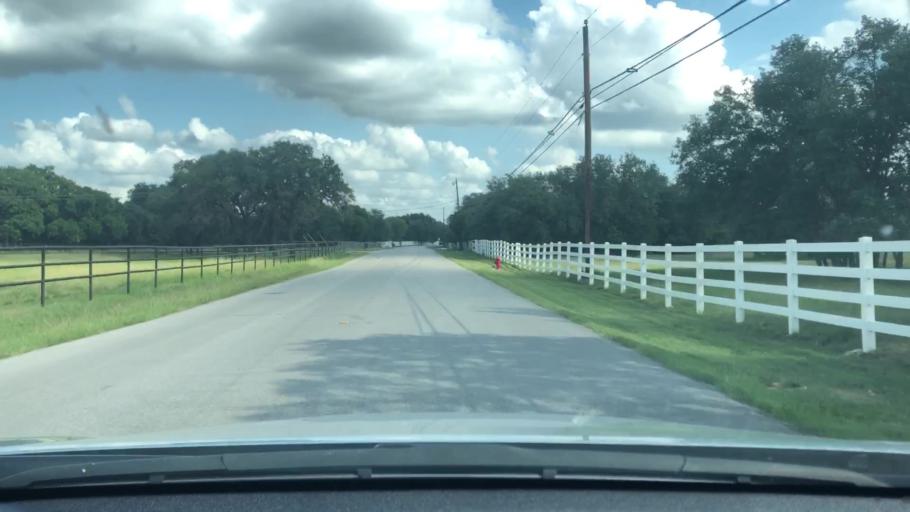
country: US
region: Texas
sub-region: Bexar County
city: Fair Oaks Ranch
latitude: 29.7629
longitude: -98.6287
